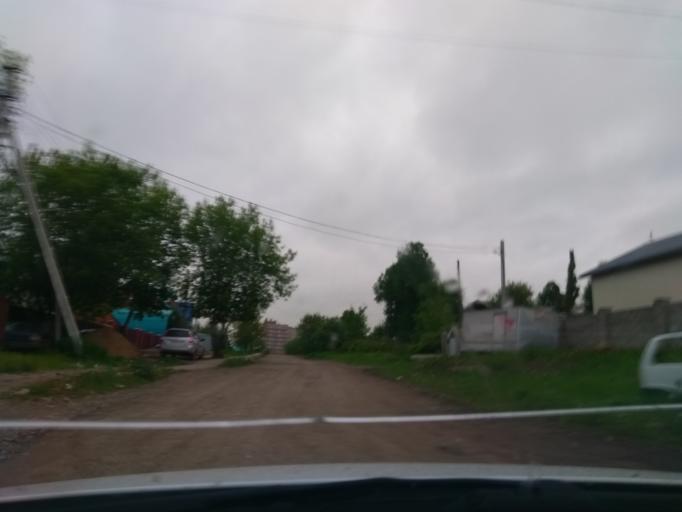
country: RU
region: Perm
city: Froly
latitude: 57.9186
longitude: 56.2677
